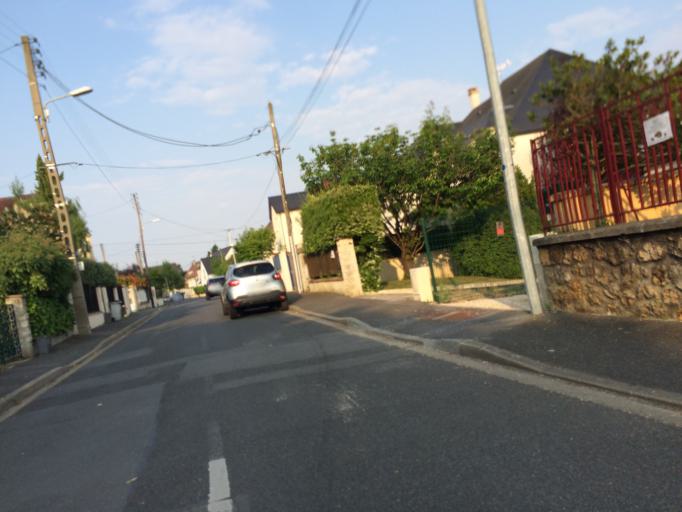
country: FR
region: Ile-de-France
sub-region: Departement de l'Essonne
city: Verrieres-le-Buisson
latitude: 48.7396
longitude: 2.2631
